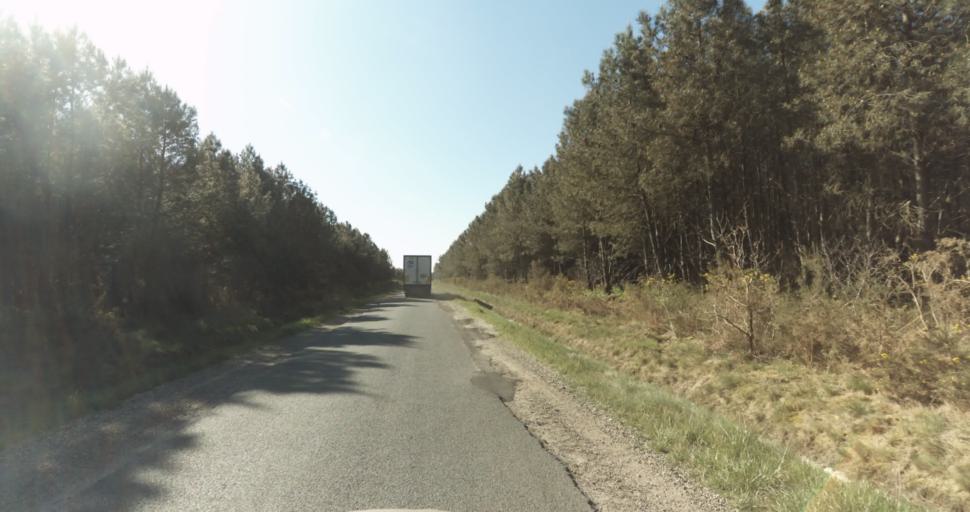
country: FR
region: Aquitaine
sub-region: Departement de la Gironde
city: Marcheprime
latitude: 44.7555
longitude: -0.8502
